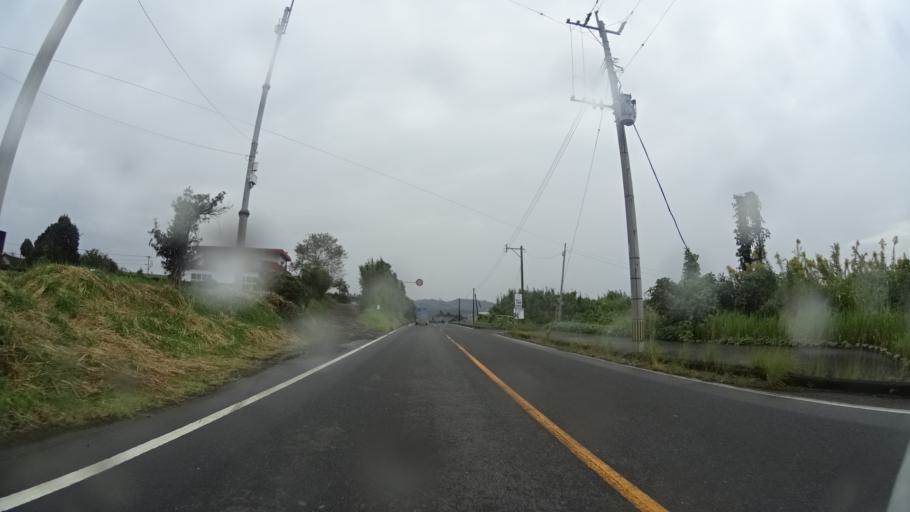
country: JP
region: Kagoshima
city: Kajiki
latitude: 31.8071
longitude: 130.6776
